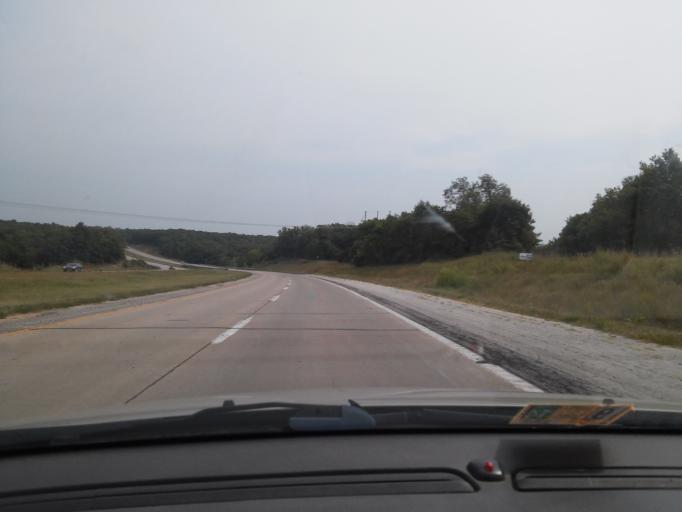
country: US
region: Missouri
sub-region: Callaway County
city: Fulton
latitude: 38.9678
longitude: -91.9016
